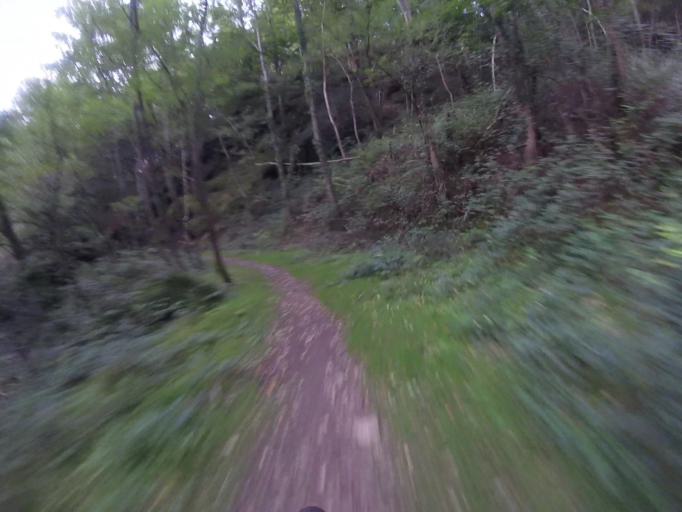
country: ES
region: Basque Country
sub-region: Provincia de Guipuzcoa
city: Errenteria
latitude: 43.2735
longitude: -1.8407
